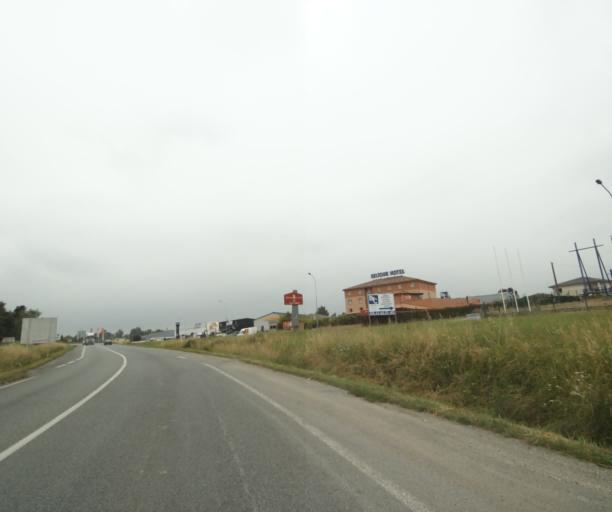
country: FR
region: Midi-Pyrenees
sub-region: Departement du Tarn-et-Garonne
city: Bressols
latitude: 43.9816
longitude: 1.3311
